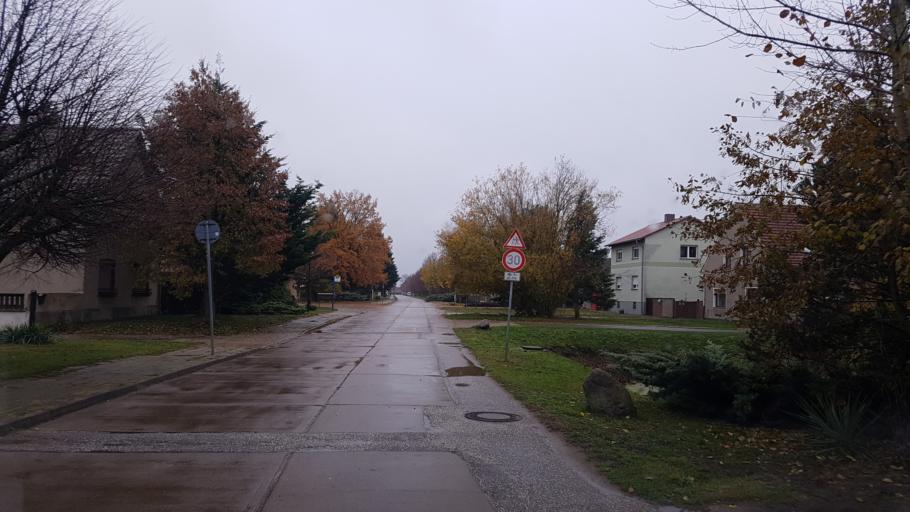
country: DE
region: Brandenburg
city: Herzberg
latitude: 51.6587
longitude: 13.2237
